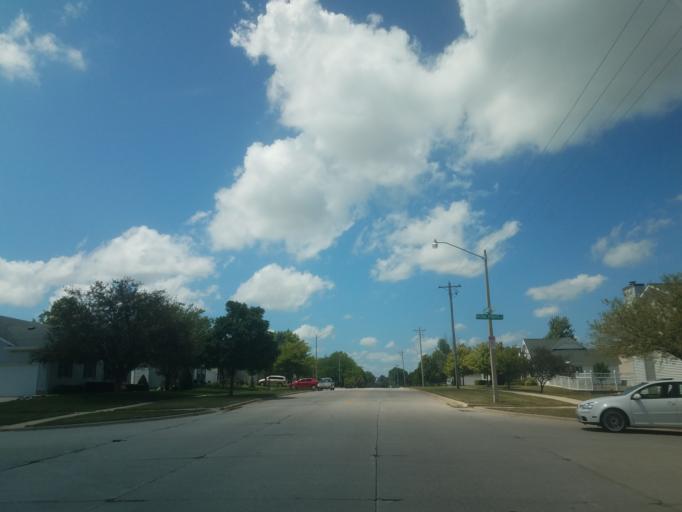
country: US
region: Illinois
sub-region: McLean County
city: Normal
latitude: 40.4958
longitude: -88.9304
